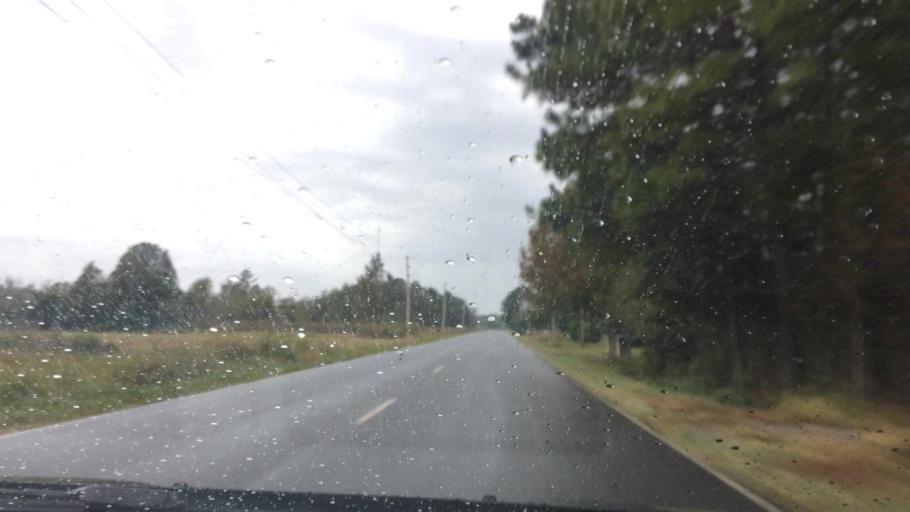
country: US
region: North Carolina
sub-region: Pitt County
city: Grifton
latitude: 35.3996
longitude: -77.4066
